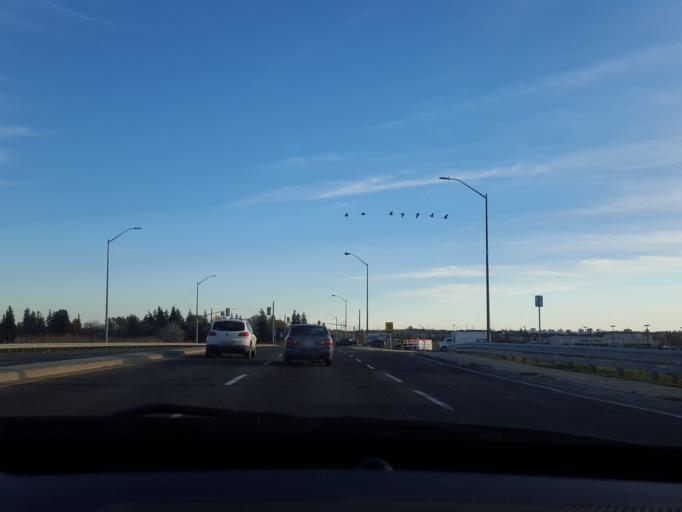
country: CA
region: Ontario
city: Markham
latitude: 43.8745
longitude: -79.2132
